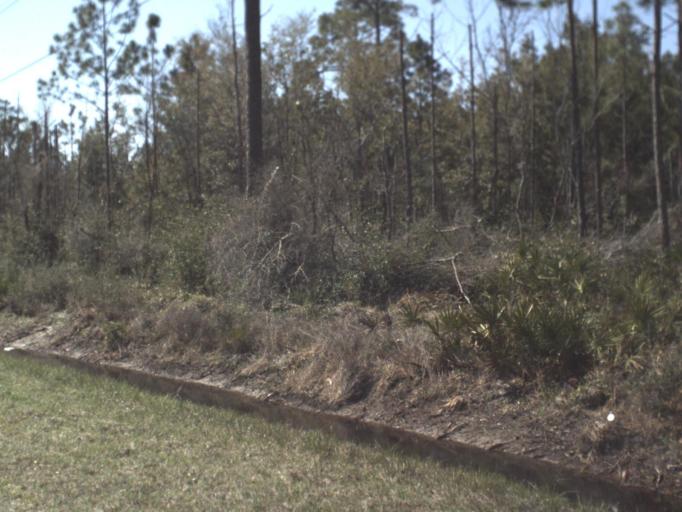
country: US
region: Florida
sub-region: Franklin County
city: Carrabelle
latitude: 29.8658
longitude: -84.6187
